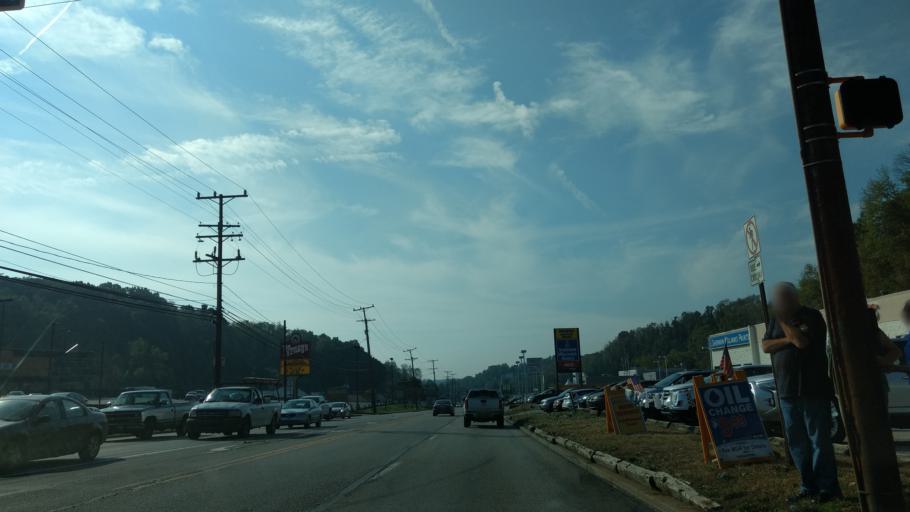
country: US
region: Pennsylvania
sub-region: Allegheny County
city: Pleasant Hills
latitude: 40.3311
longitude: -79.9457
